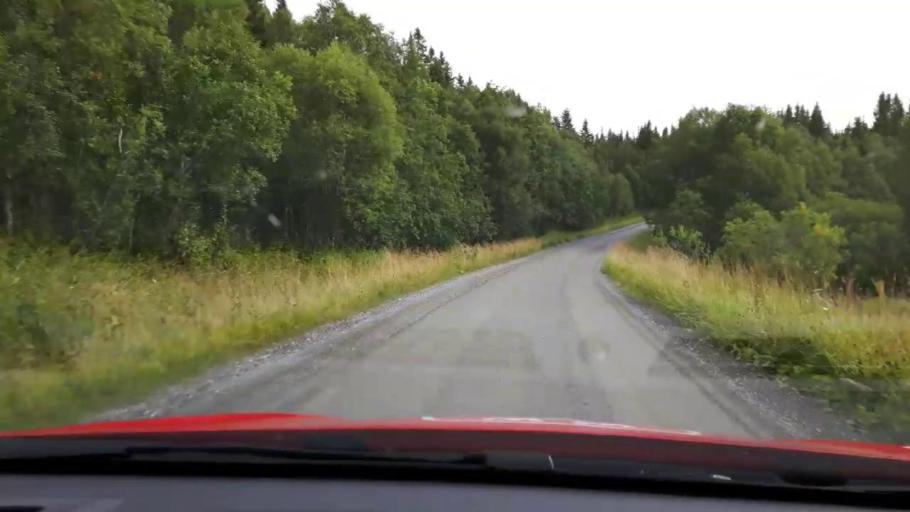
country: SE
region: Jaemtland
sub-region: Are Kommun
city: Are
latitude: 63.7395
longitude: 13.0133
